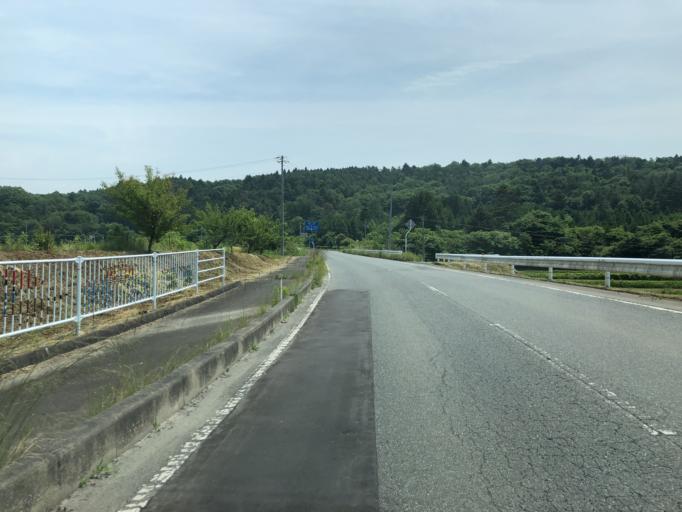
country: JP
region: Fukushima
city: Namie
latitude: 37.5971
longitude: 140.9198
